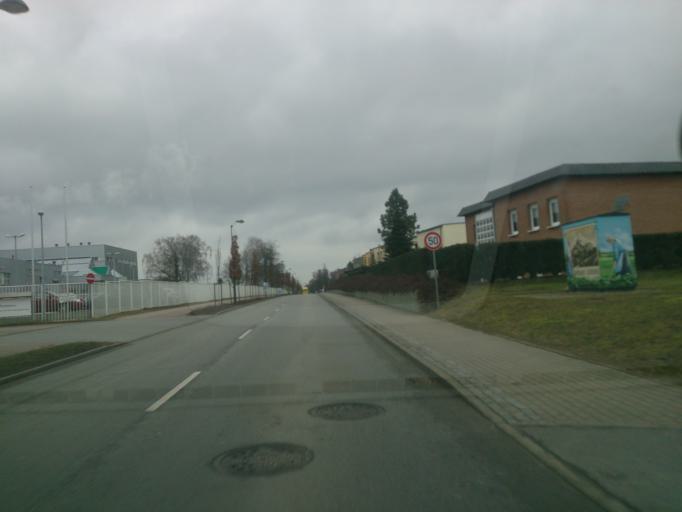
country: DE
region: Mecklenburg-Vorpommern
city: Wackerow
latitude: 53.7028
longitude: 12.9104
